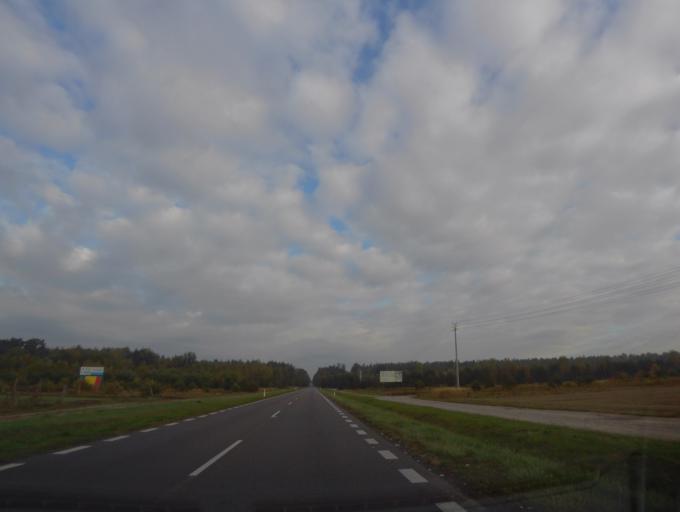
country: PL
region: Lublin Voivodeship
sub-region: Powiat bilgorajski
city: Bilgoraj
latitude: 50.5821
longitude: 22.6849
